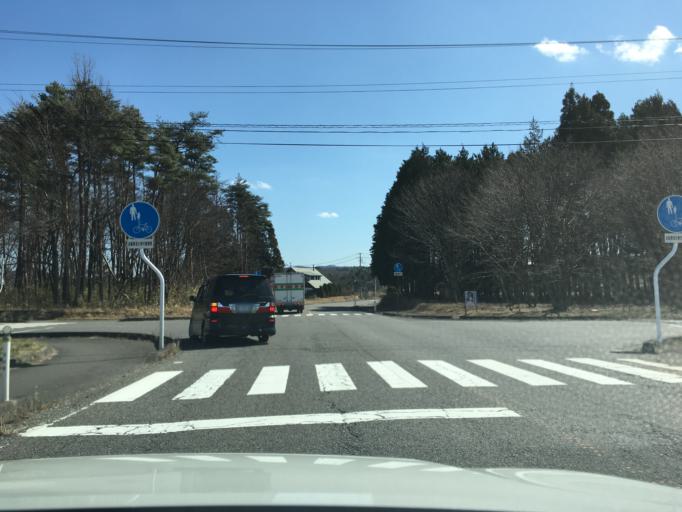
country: JP
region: Tochigi
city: Kuroiso
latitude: 37.0994
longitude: 140.1883
